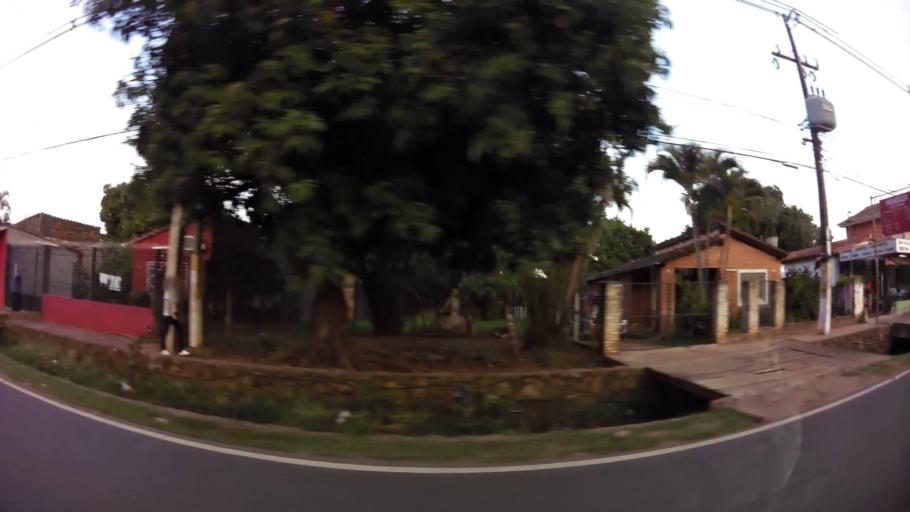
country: PY
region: Central
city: San Lorenzo
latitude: -25.3762
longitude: -57.4924
